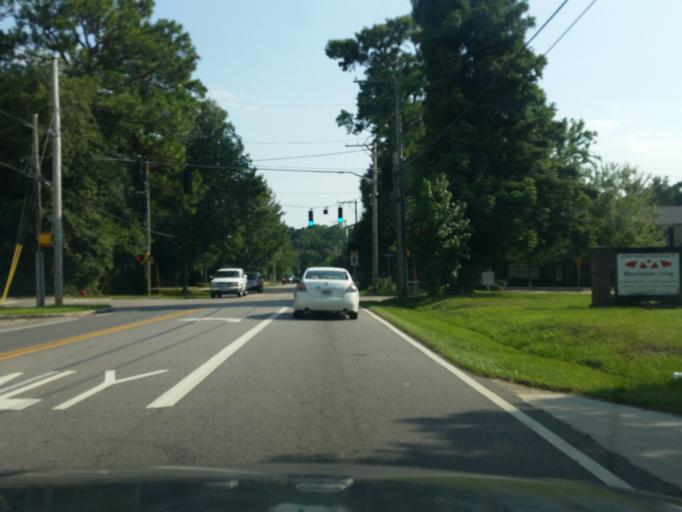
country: US
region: Alabama
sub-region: Baldwin County
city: Fairhope
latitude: 30.5330
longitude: -87.9017
